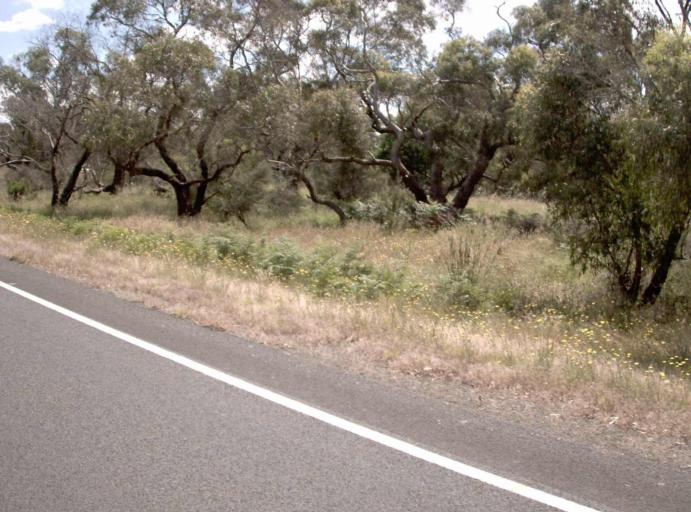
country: AU
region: Victoria
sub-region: Cardinia
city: Koo-Wee-Rup
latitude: -38.3474
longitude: 145.5581
